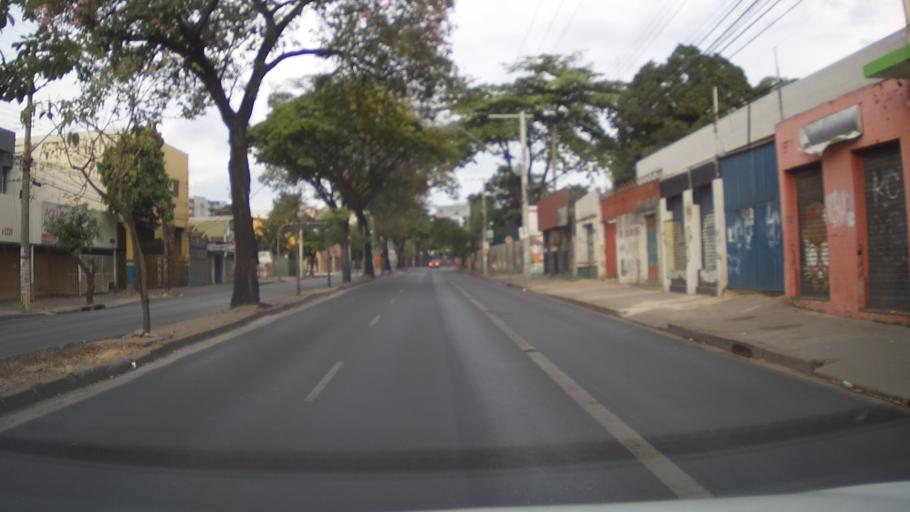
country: BR
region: Minas Gerais
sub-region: Belo Horizonte
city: Belo Horizonte
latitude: -19.9121
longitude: -43.9711
